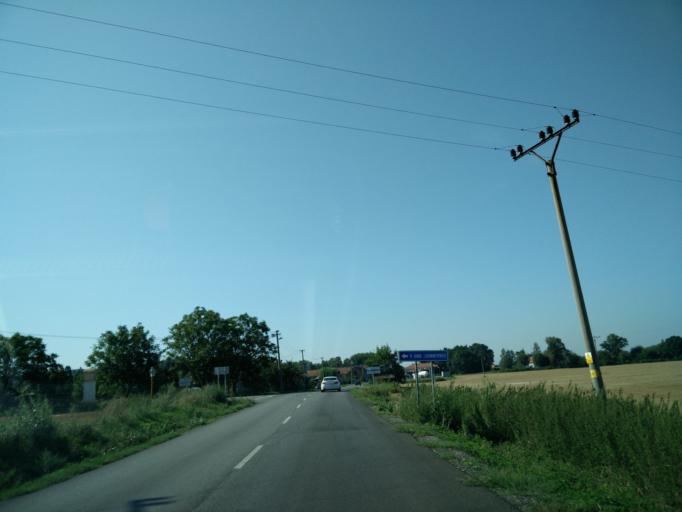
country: SK
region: Nitriansky
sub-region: Okres Nitra
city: Nitra
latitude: 48.4276
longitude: 18.1262
